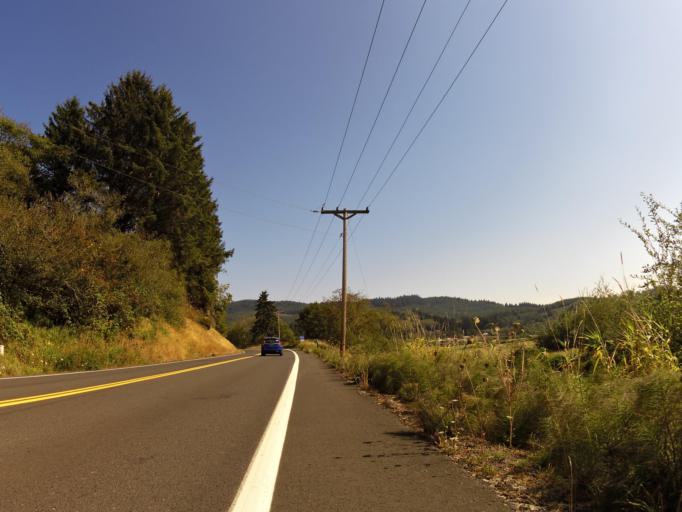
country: US
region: Oregon
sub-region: Tillamook County
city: Pacific City
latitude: 45.1799
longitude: -123.9340
